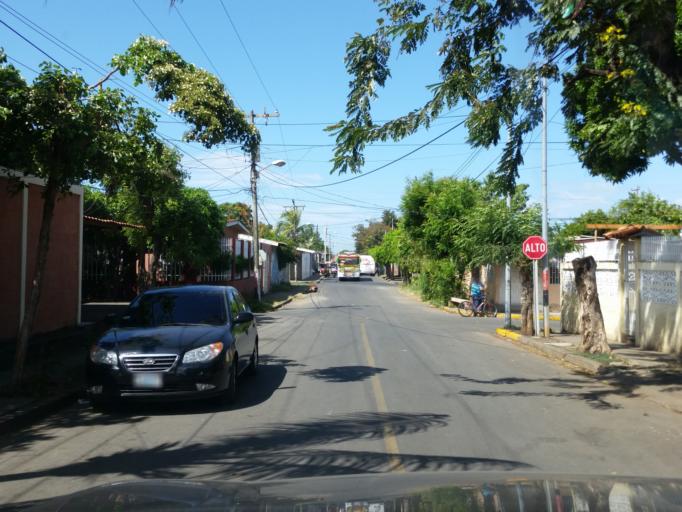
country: NI
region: Managua
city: Managua
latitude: 12.1204
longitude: -86.2305
